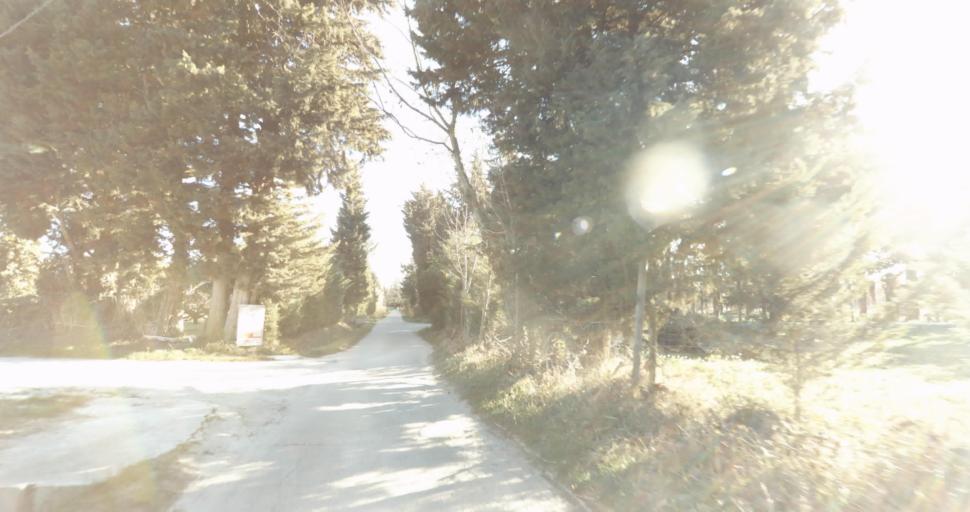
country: FR
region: Provence-Alpes-Cote d'Azur
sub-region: Departement des Bouches-du-Rhone
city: Barbentane
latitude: 43.9170
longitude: 4.7464
